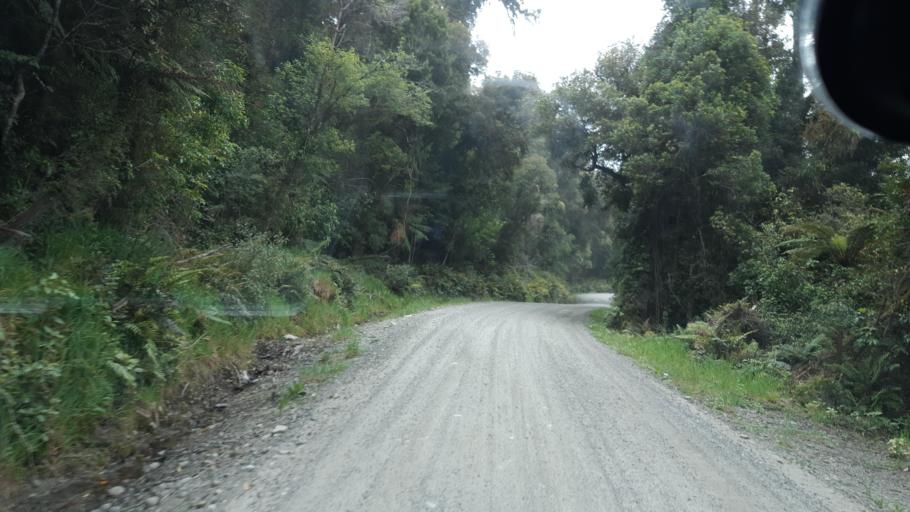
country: NZ
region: West Coast
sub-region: Grey District
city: Greymouth
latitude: -42.6375
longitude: 171.3868
